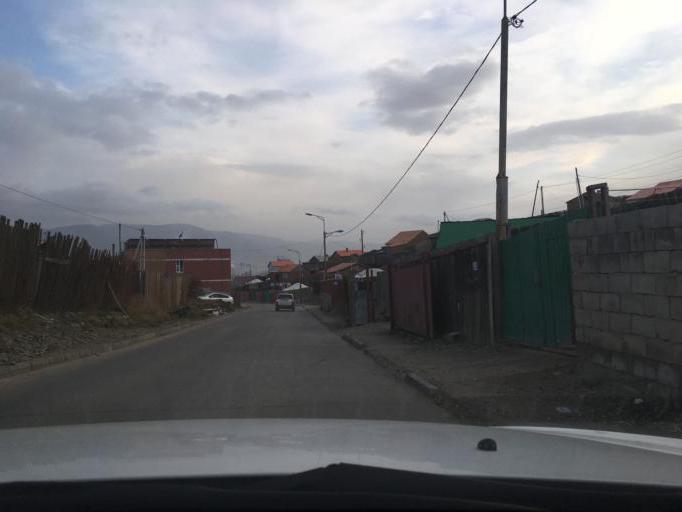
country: MN
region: Ulaanbaatar
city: Ulaanbaatar
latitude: 47.9311
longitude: 106.8582
